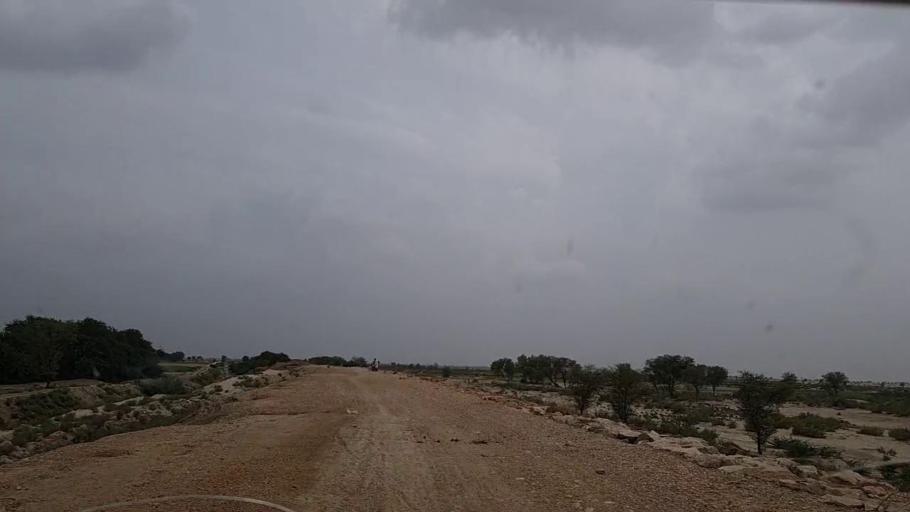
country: PK
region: Sindh
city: Johi
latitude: 26.7220
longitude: 67.5787
